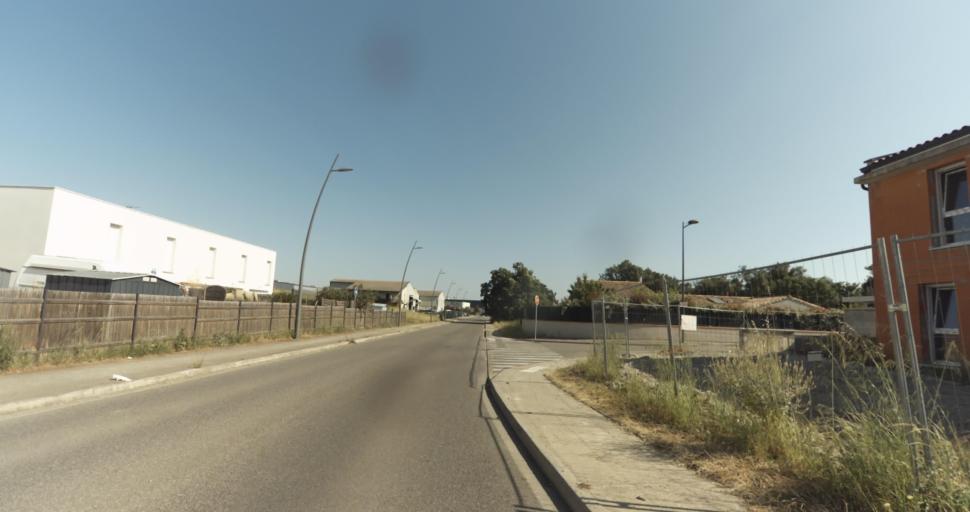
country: FR
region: Midi-Pyrenees
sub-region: Departement de la Haute-Garonne
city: Tournefeuille
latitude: 43.5897
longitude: 1.2989
